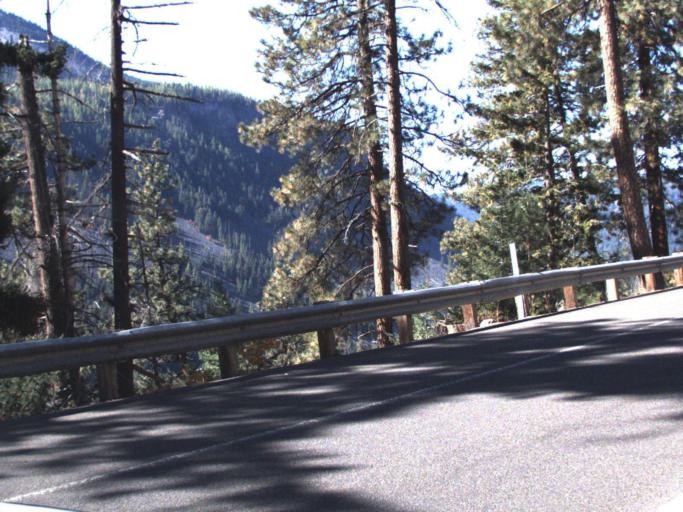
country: US
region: Washington
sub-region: Yakima County
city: Tieton
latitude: 46.6532
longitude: -121.3000
